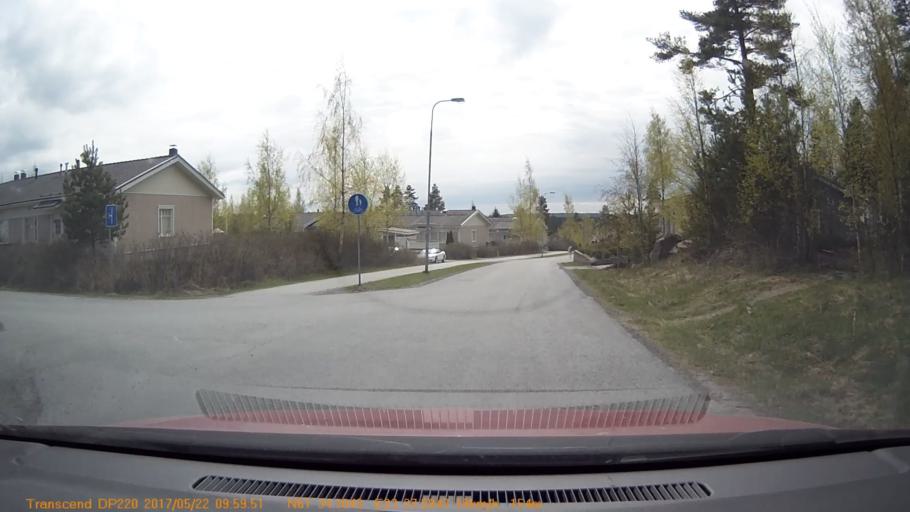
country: FI
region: Pirkanmaa
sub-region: Tampere
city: Yloejaervi
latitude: 61.5786
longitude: 23.6263
